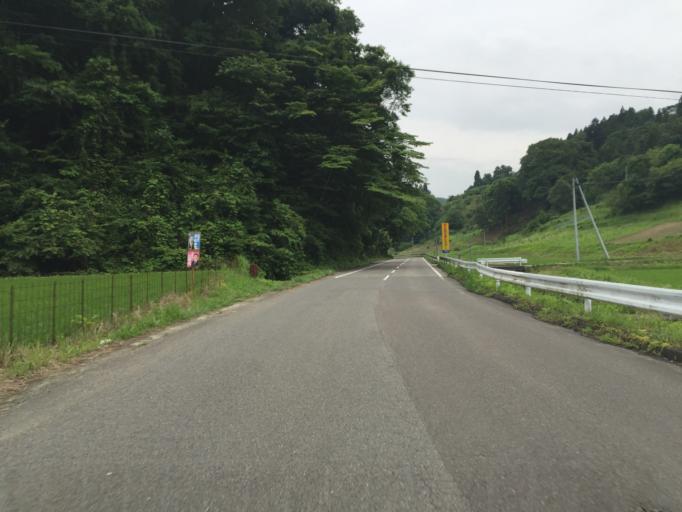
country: JP
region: Fukushima
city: Nihommatsu
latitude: 37.6268
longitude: 140.5600
